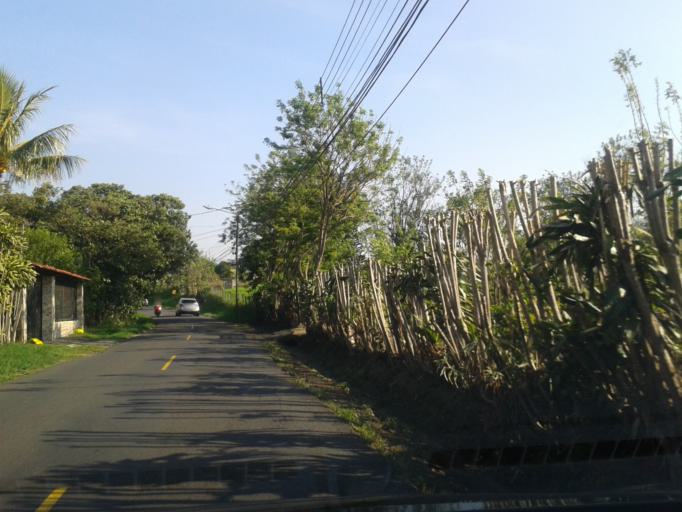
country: CR
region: Heredia
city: Mercedes
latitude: 10.0097
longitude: -84.1462
